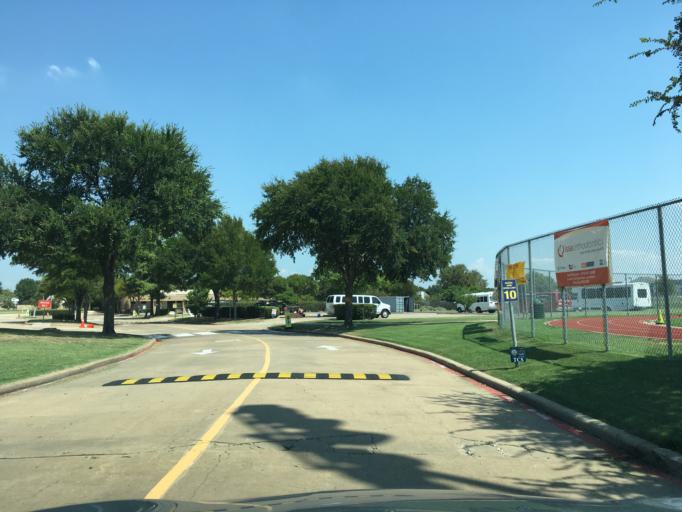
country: US
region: Texas
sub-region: Dallas County
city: Garland
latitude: 32.9459
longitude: -96.6693
